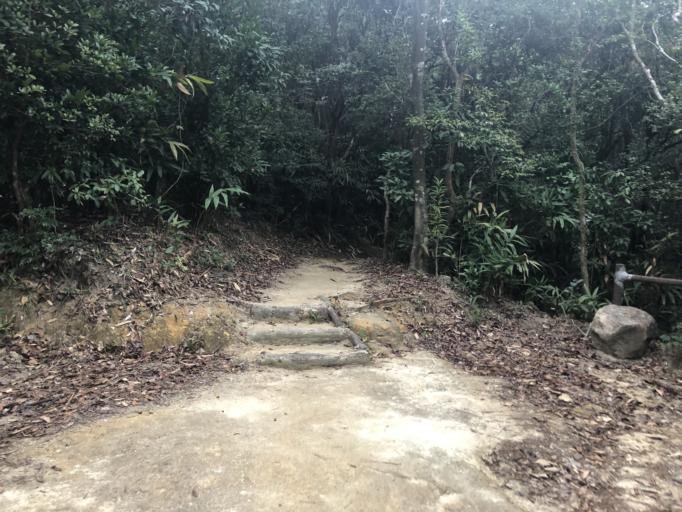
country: HK
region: Wanchai
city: Wan Chai
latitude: 22.2793
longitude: 114.2091
